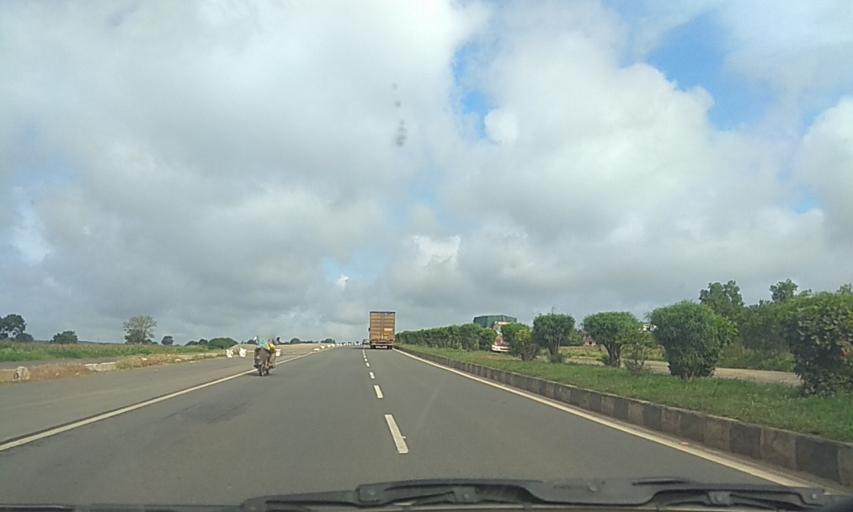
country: IN
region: Karnataka
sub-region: Haveri
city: Shiggaon
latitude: 15.0064
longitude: 75.2016
